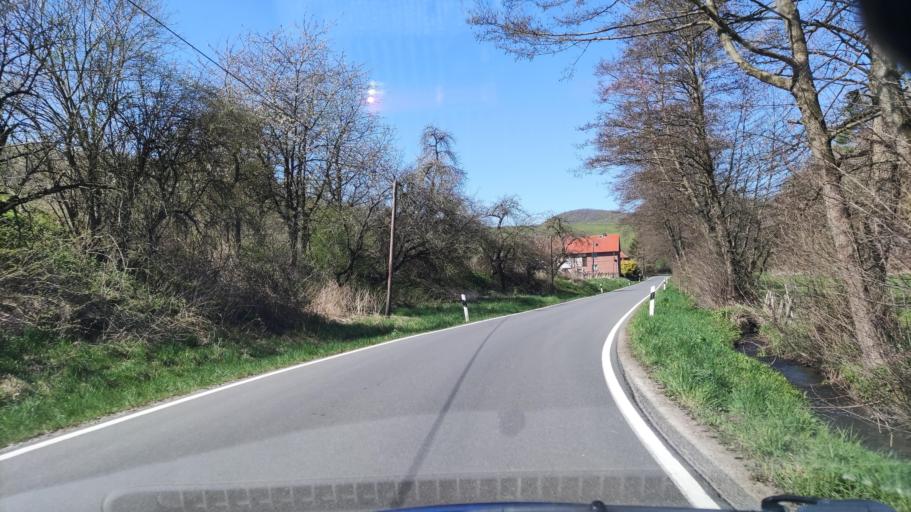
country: DE
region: Lower Saxony
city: Eimen
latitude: 51.9169
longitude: 9.7723
